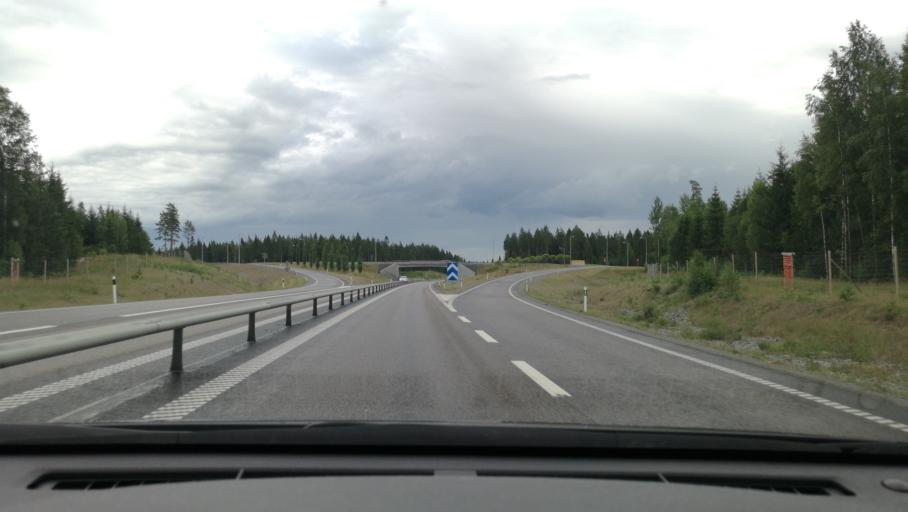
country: SE
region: Soedermanland
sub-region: Katrineholms Kommun
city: Katrineholm
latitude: 58.9958
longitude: 16.2574
